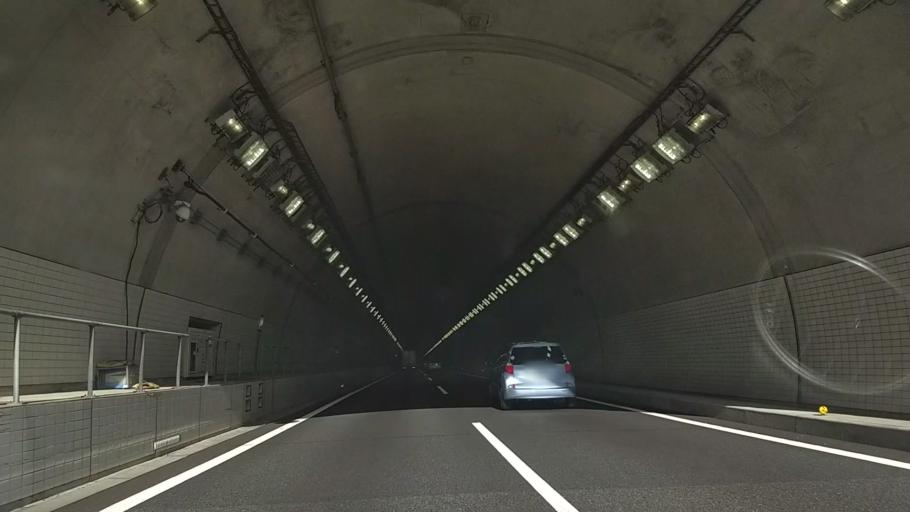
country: JP
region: Tokyo
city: Hachioji
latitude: 35.5964
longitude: 139.2789
